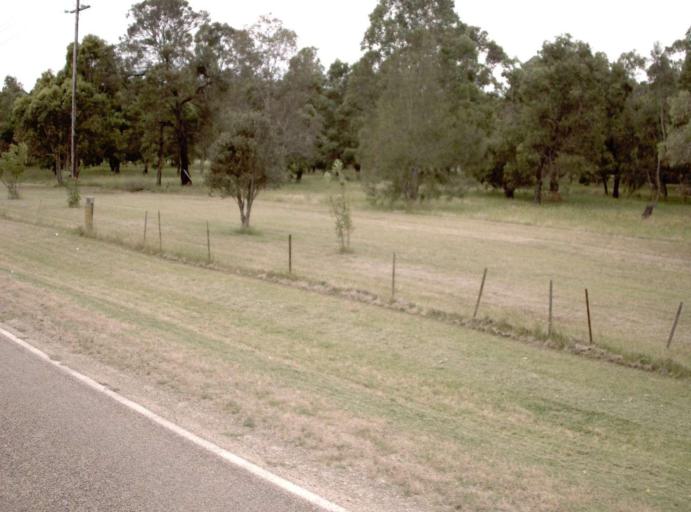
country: AU
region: Victoria
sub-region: East Gippsland
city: Bairnsdale
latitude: -37.8357
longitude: 147.4323
